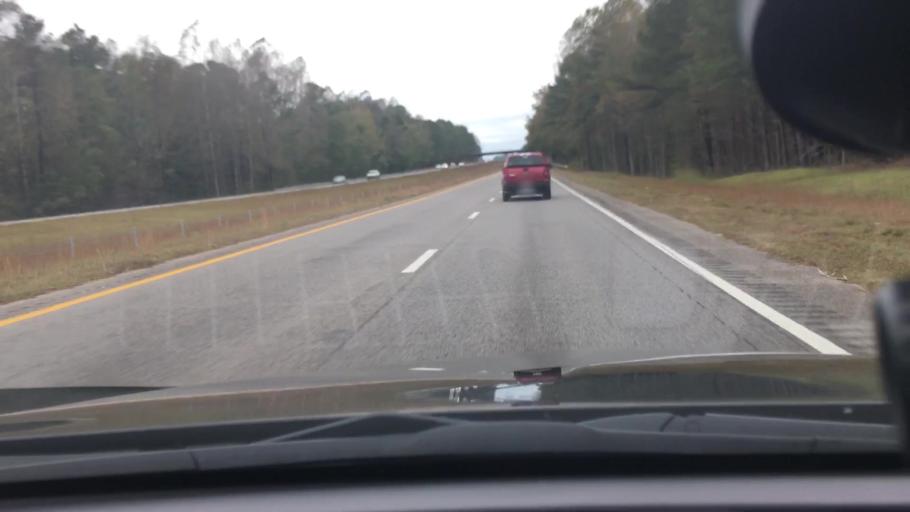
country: US
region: North Carolina
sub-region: Wake County
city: Zebulon
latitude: 35.8126
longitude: -78.2329
